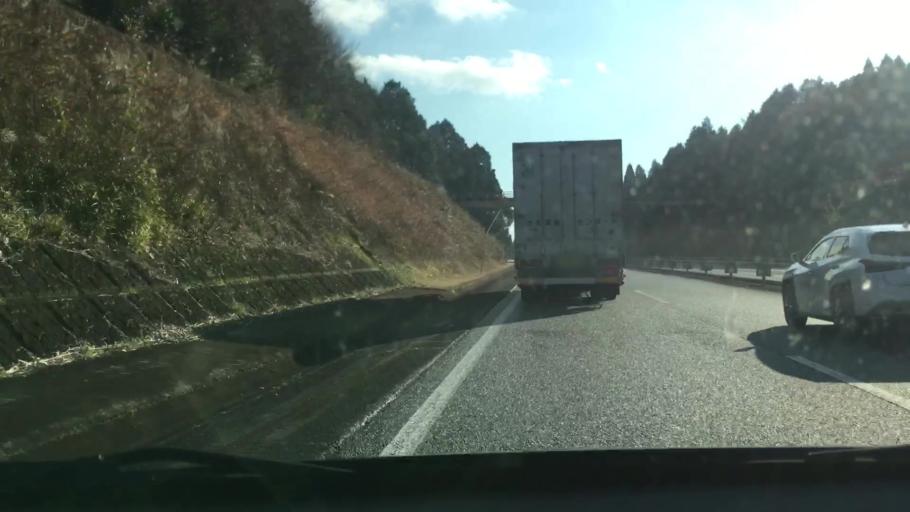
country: JP
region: Kagoshima
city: Okuchi-shinohara
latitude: 31.9294
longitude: 130.7049
